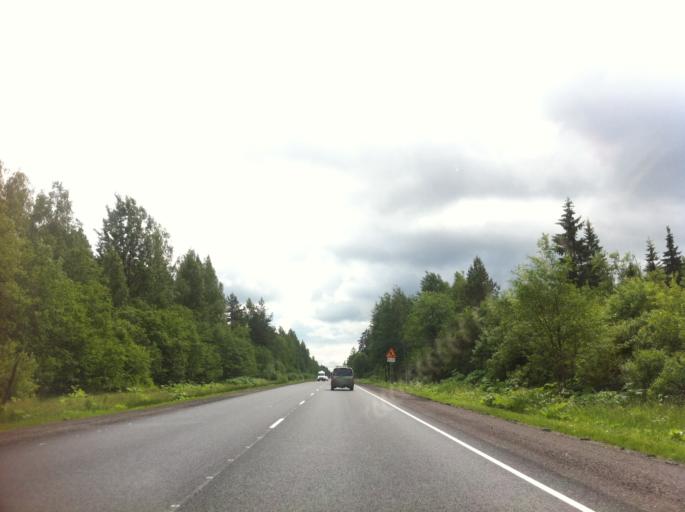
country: RU
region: Leningrad
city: Rozhdestveno
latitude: 59.2270
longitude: 29.9273
